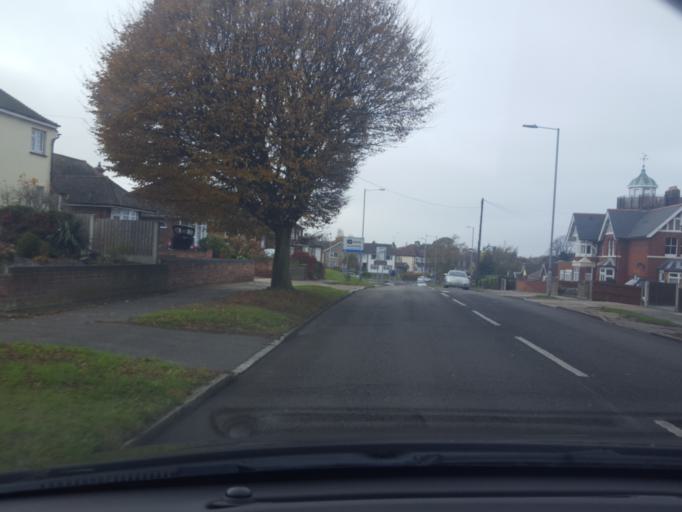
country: GB
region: England
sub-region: Essex
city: Clacton-on-Sea
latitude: 51.8025
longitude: 1.1732
